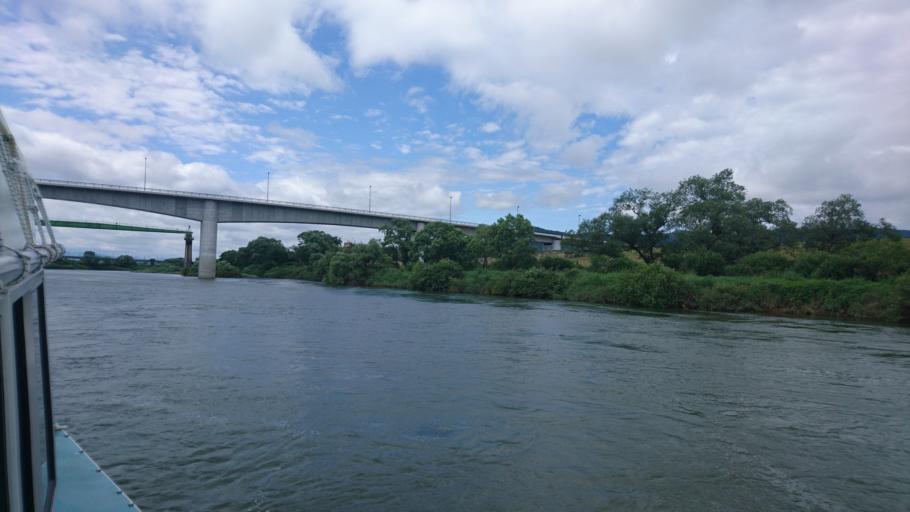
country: JP
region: Iwate
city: Ichinoseki
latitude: 38.9535
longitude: 141.1611
